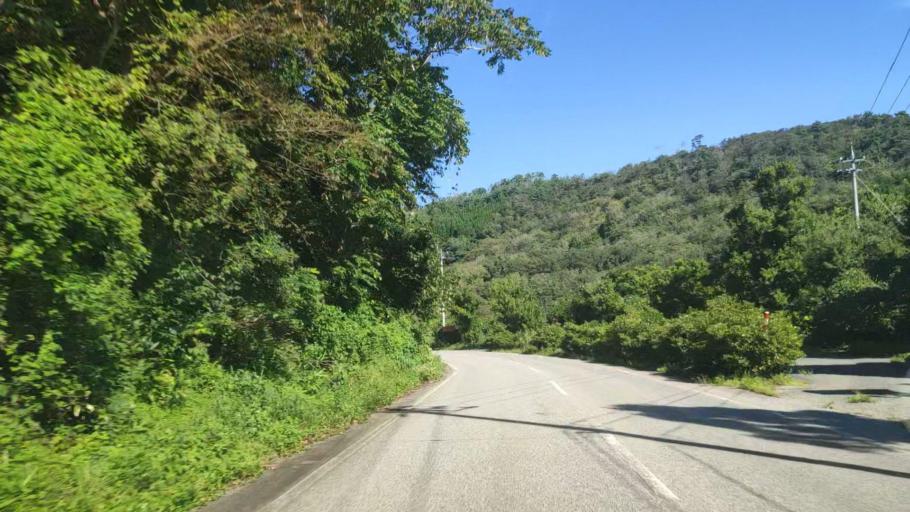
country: JP
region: Ishikawa
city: Nanao
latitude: 37.2148
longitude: 136.7066
